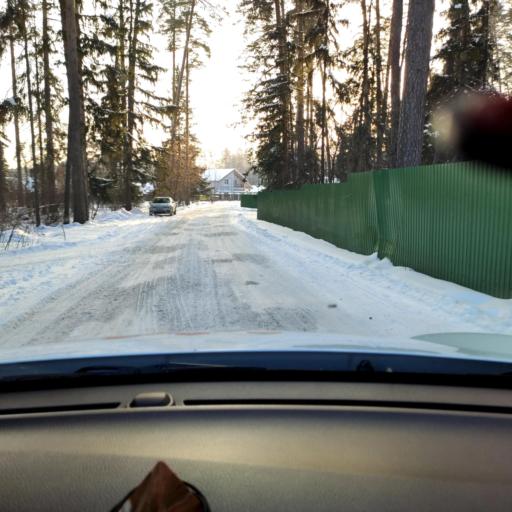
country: RU
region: Tatarstan
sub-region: Zelenodol'skiy Rayon
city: Vasil'yevo
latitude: 55.9101
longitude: 48.7477
